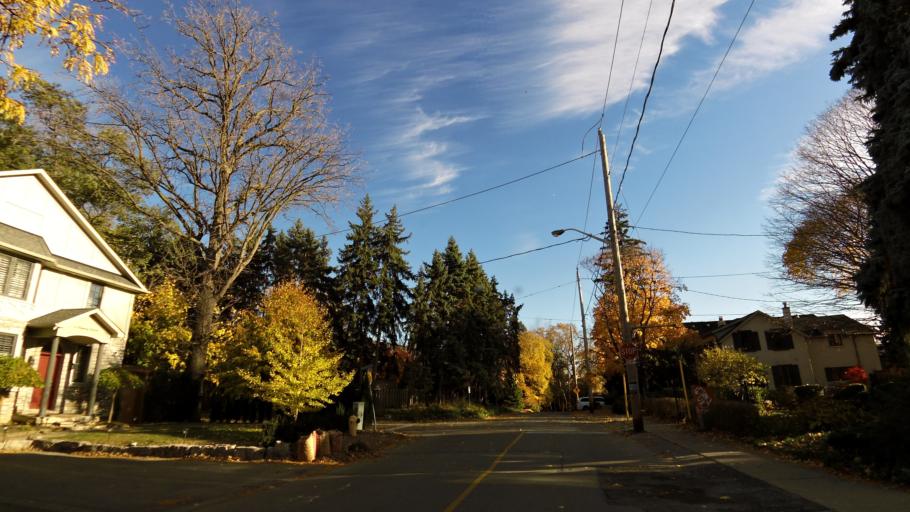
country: CA
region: Ontario
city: Etobicoke
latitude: 43.6589
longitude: -79.5036
